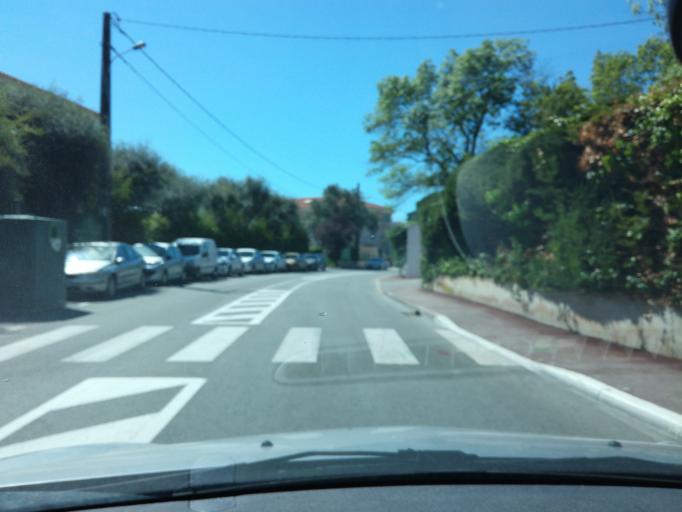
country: FR
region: Provence-Alpes-Cote d'Azur
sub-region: Departement des Alpes-Maritimes
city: Mandelieu-la-Napoule
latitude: 43.5564
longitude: 6.9607
